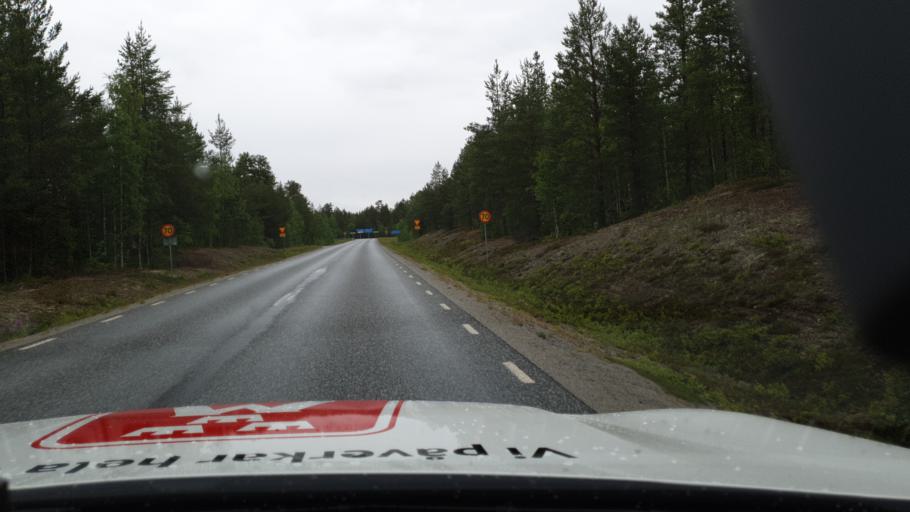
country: SE
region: Vaesterbotten
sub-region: Vilhelmina Kommun
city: Vilhelmina
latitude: 64.4331
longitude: 16.8039
